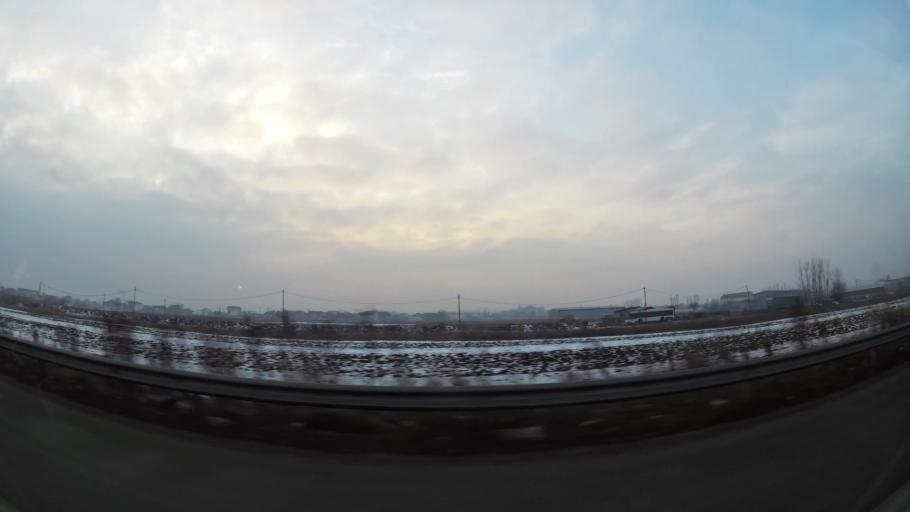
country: MK
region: Aracinovo
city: Arachinovo
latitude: 42.0148
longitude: 21.5342
